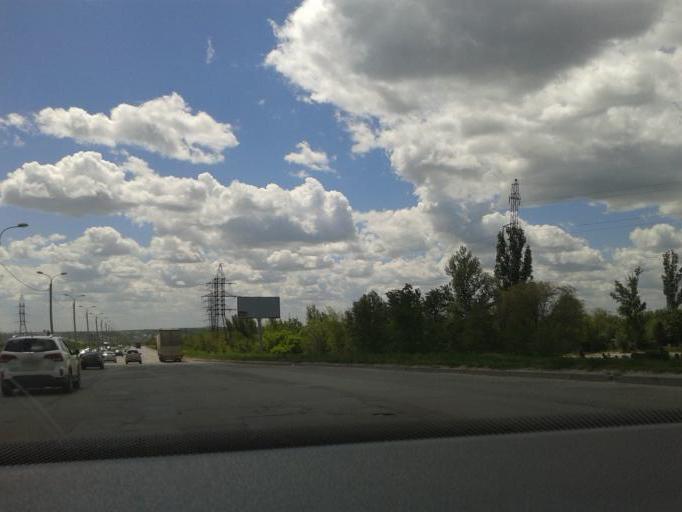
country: RU
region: Volgograd
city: Volgograd
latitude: 48.7476
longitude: 44.4674
